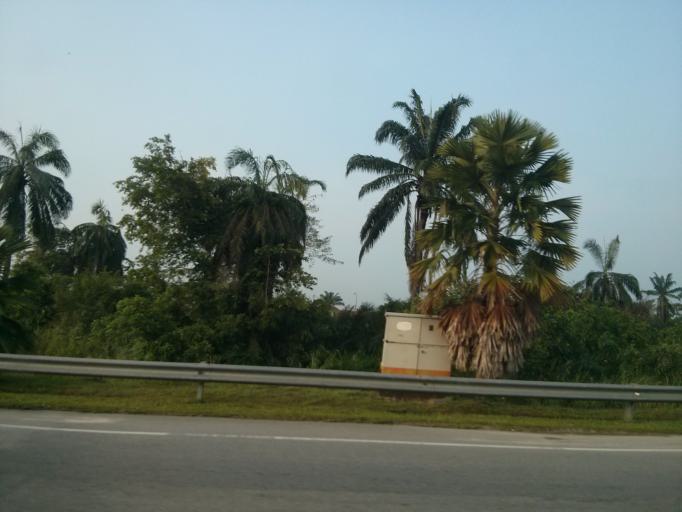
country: MY
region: Putrajaya
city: Putrajaya
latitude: 2.8611
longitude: 101.6904
